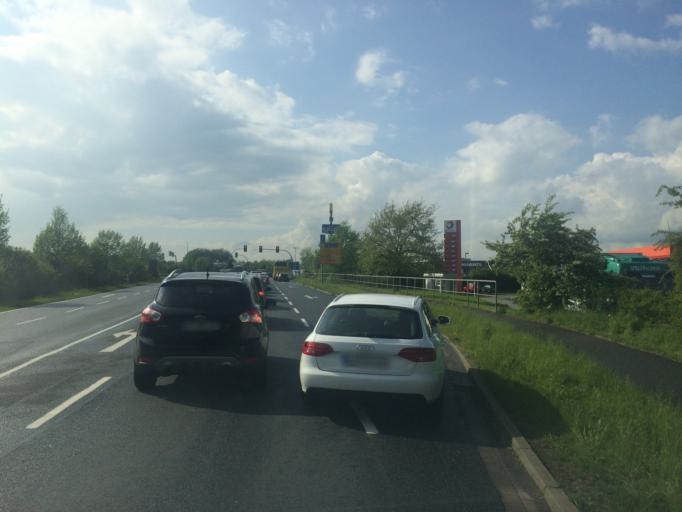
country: DE
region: Lower Saxony
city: Bad Nenndorf
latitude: 52.3325
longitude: 9.4150
